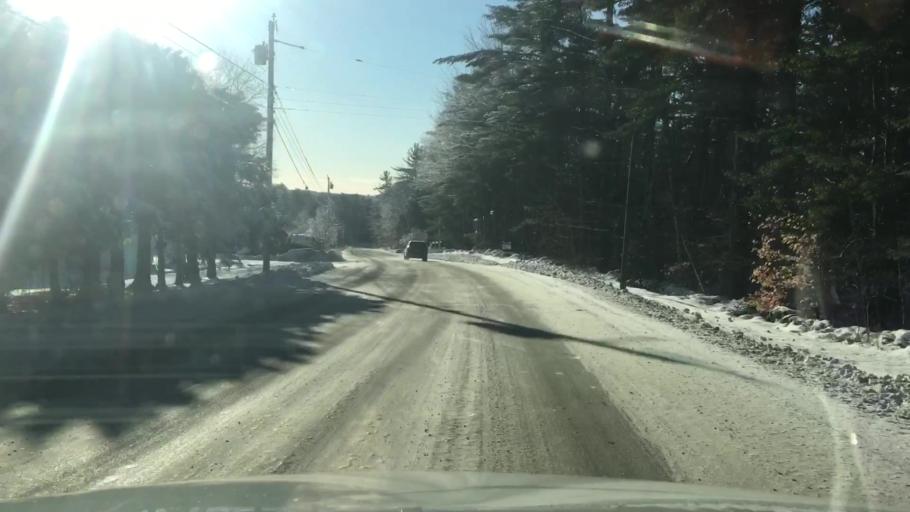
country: US
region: Maine
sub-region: Kennebec County
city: Readfield
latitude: 44.4061
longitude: -69.9651
